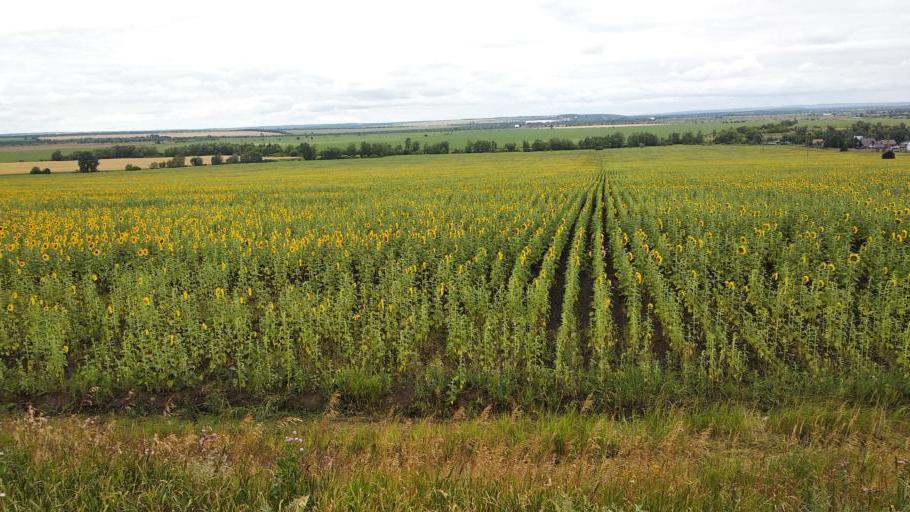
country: RU
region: Samara
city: Mirnyy
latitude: 53.4503
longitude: 50.2488
